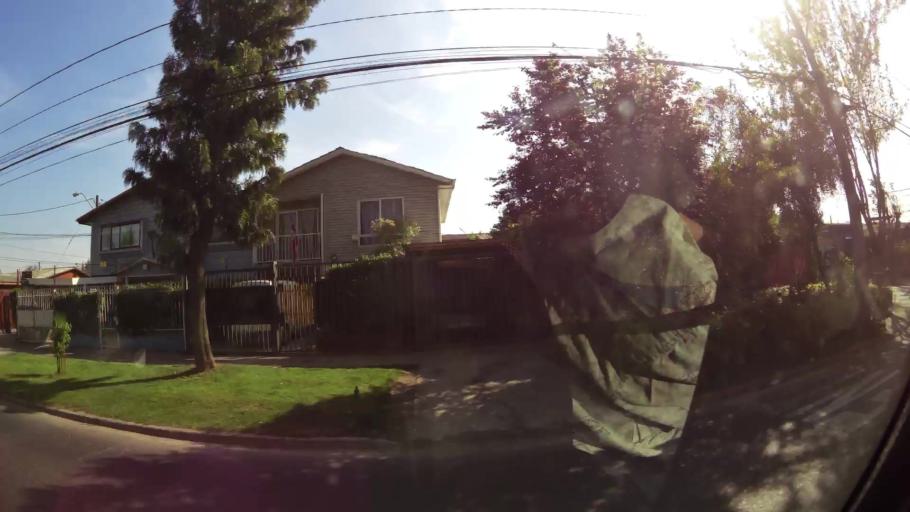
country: CL
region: Santiago Metropolitan
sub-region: Provincia de Santiago
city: Lo Prado
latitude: -33.4675
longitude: -70.7416
